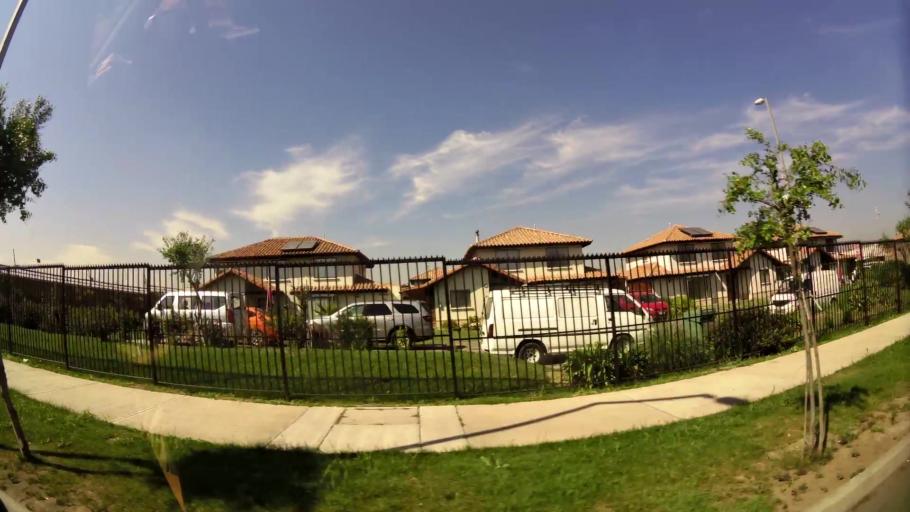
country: CL
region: Santiago Metropolitan
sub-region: Provincia de Talagante
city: Penaflor
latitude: -33.5598
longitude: -70.8315
